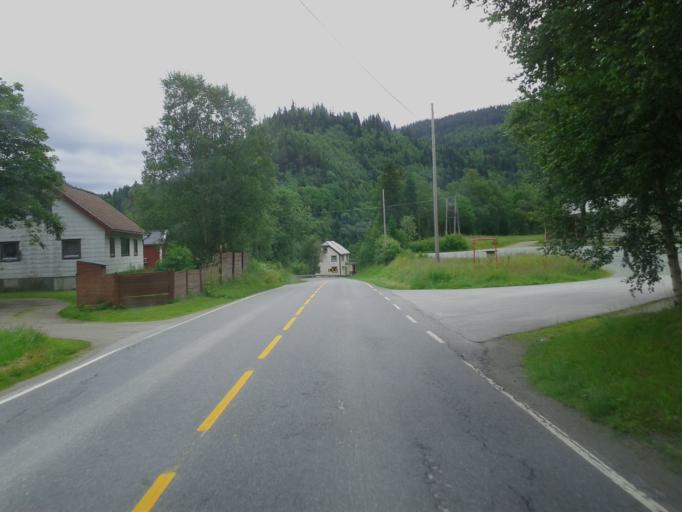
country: NO
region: Sor-Trondelag
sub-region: Midtre Gauldal
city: Storen
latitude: 62.9931
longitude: 10.4906
